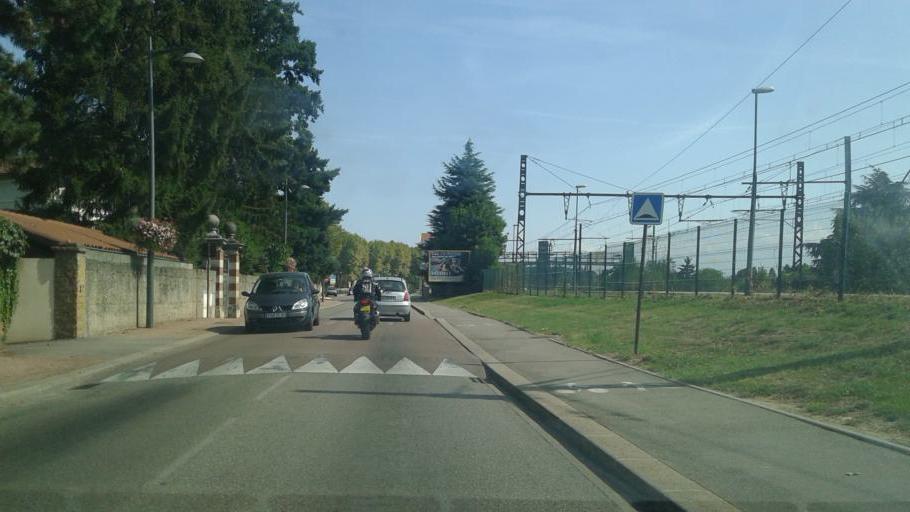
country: FR
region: Rhone-Alpes
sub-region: Departement de l'Ain
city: Montluel
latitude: 45.8471
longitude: 5.0558
